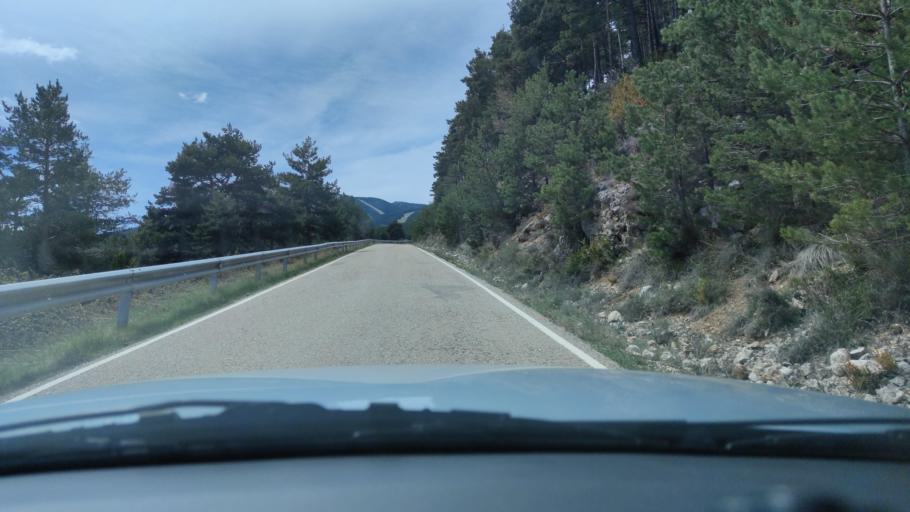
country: ES
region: Catalonia
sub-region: Provincia de Lleida
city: Gosol
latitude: 42.1954
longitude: 1.5634
